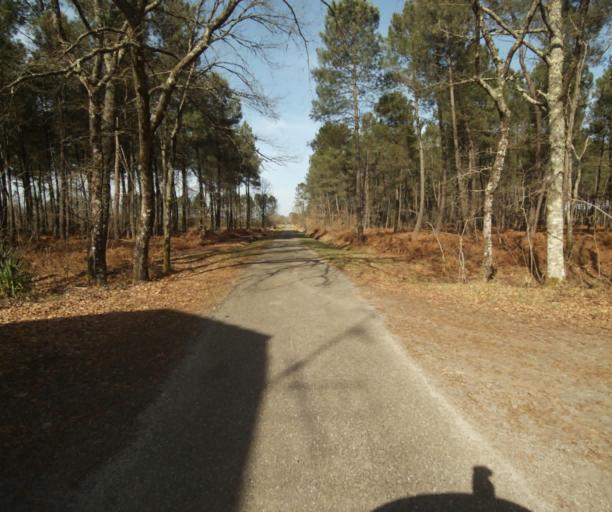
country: FR
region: Aquitaine
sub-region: Departement des Landes
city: Roquefort
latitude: 44.1418
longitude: -0.2039
